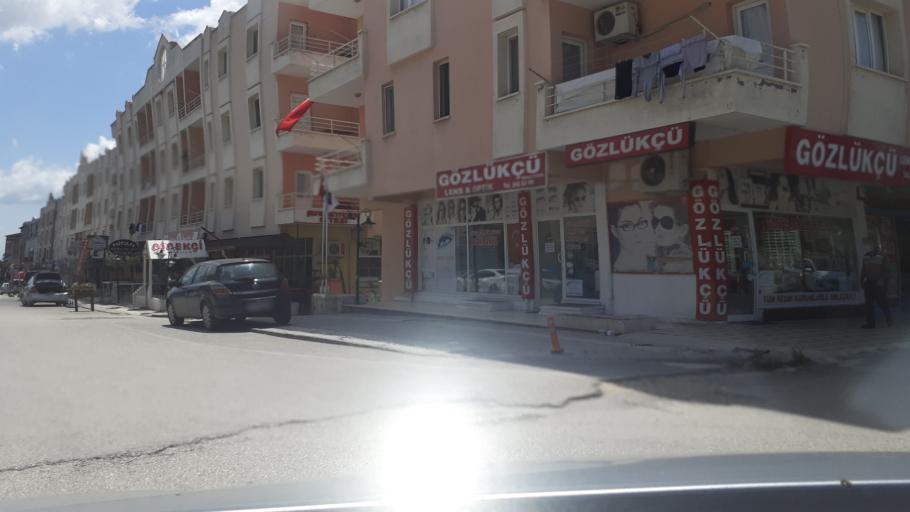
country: TR
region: Hatay
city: Anayazi
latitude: 36.3350
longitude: 36.1999
